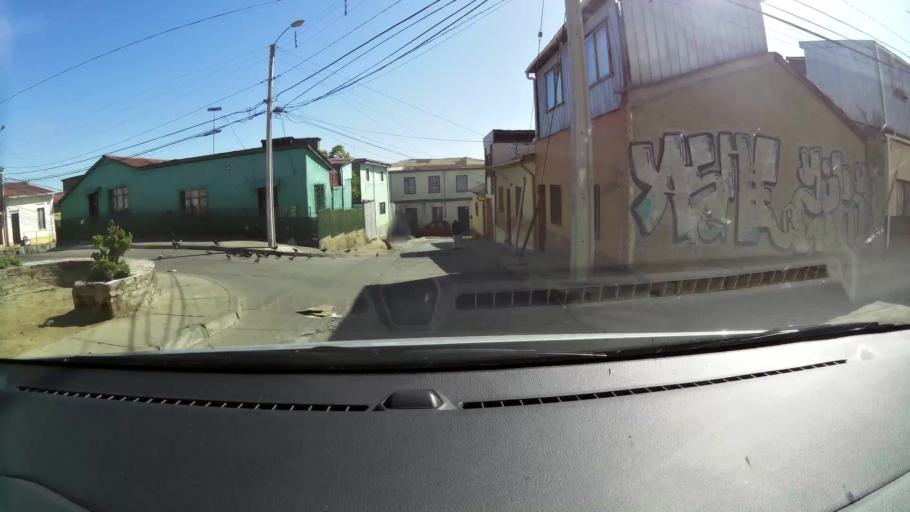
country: CL
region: Valparaiso
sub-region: Provincia de Valparaiso
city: Valparaiso
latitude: -33.0428
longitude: -71.6353
